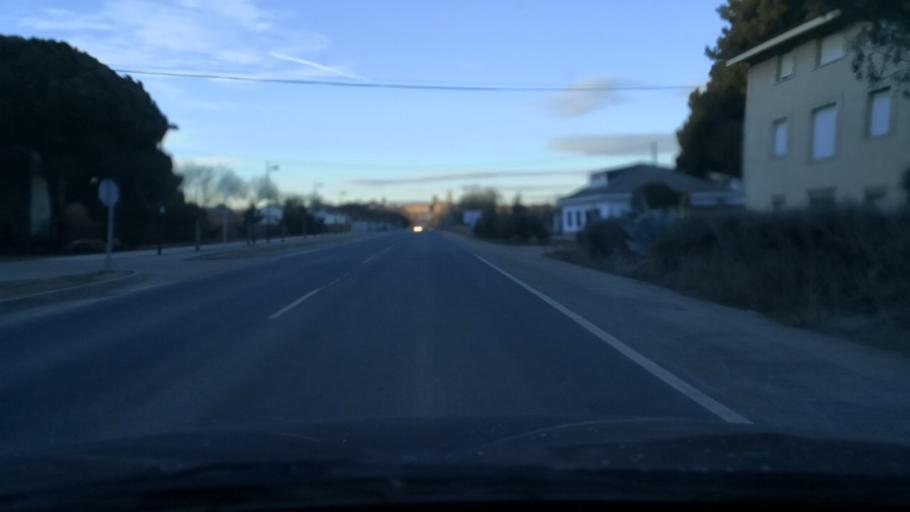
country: ES
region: Castille and Leon
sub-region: Provincia de Valladolid
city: Tordesillas
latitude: 41.4900
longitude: -4.9968
